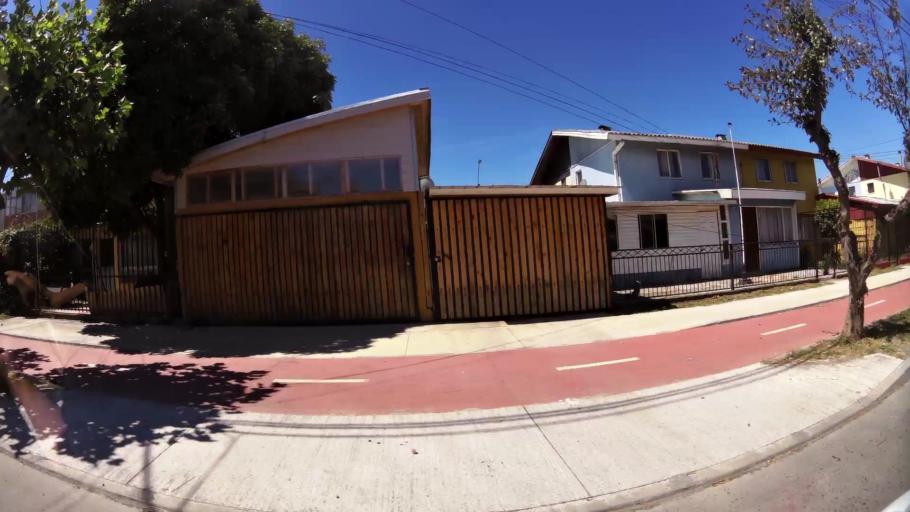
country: CL
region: Biobio
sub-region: Provincia de Concepcion
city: Talcahuano
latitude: -36.7591
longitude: -73.0953
